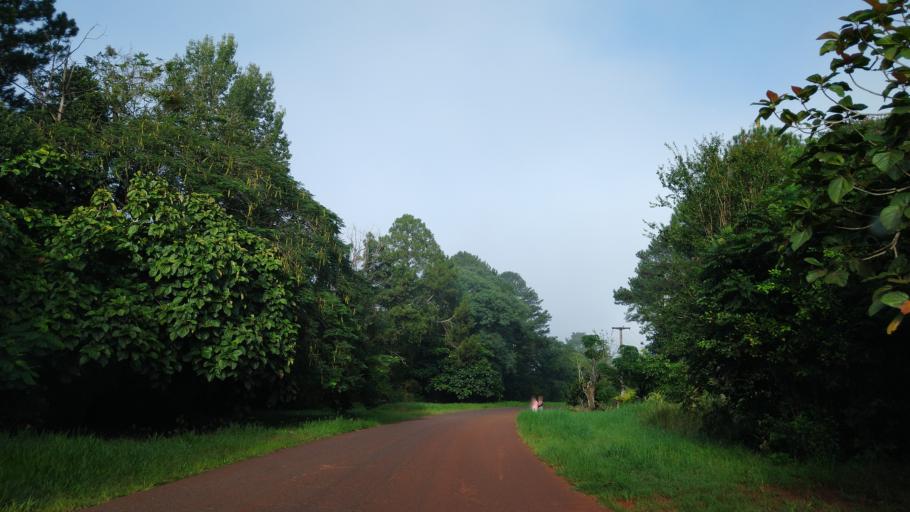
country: AR
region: Misiones
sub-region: Departamento de Montecarlo
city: Montecarlo
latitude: -26.5652
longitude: -54.7876
